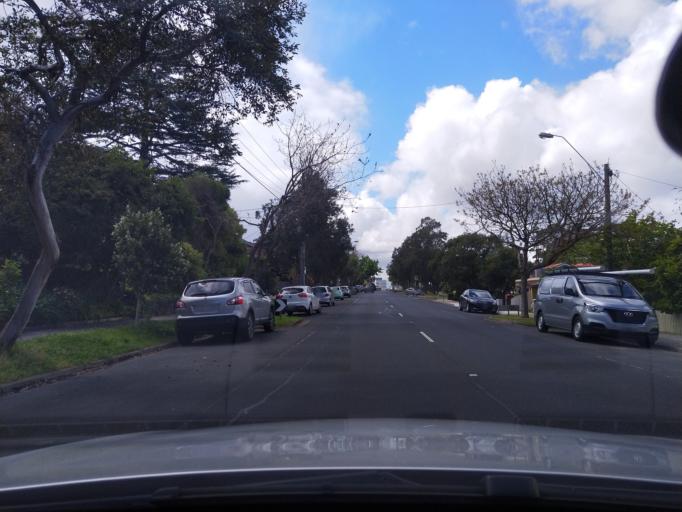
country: AU
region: Victoria
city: Rosanna
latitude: -37.7609
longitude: 145.0557
